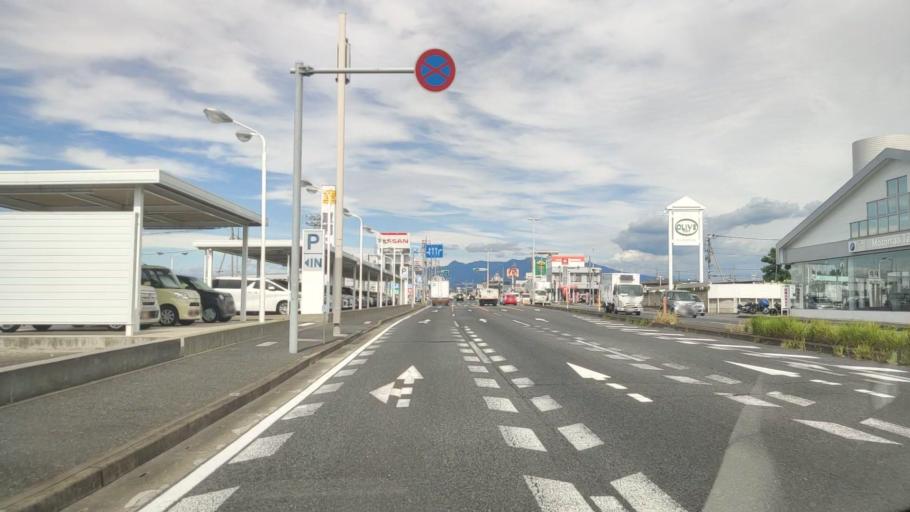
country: JP
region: Gunma
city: Takasaki
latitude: 36.3639
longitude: 139.0191
